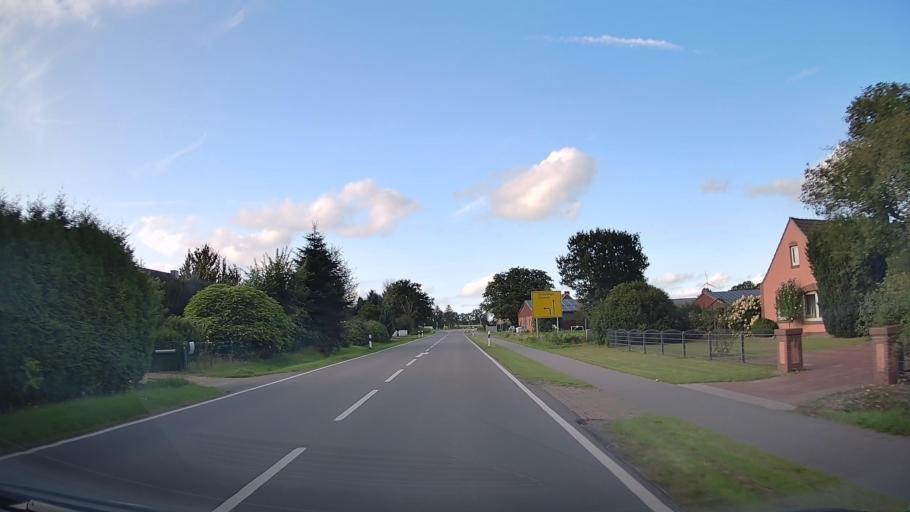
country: DE
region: Lower Saxony
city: Hilkenbrook
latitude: 53.0625
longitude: 7.7234
